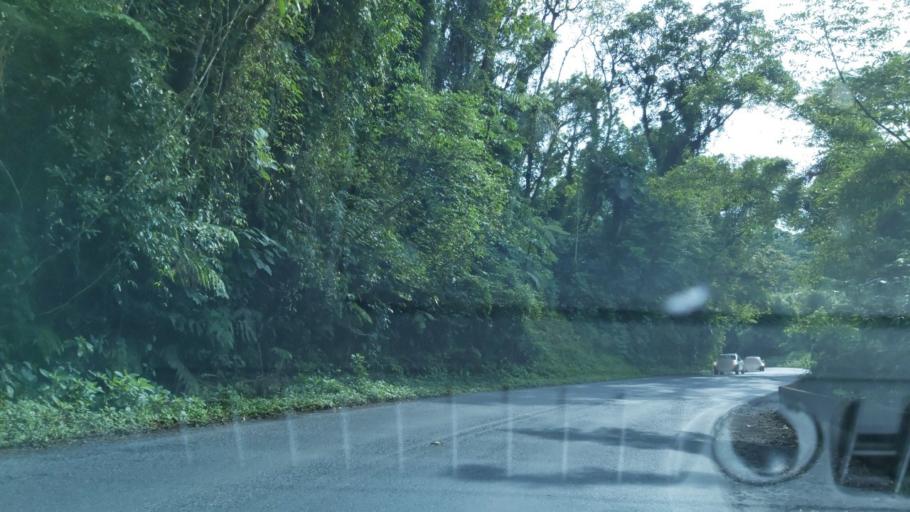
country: BR
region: Sao Paulo
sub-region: Juquia
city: Juquia
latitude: -24.0844
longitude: -47.6094
